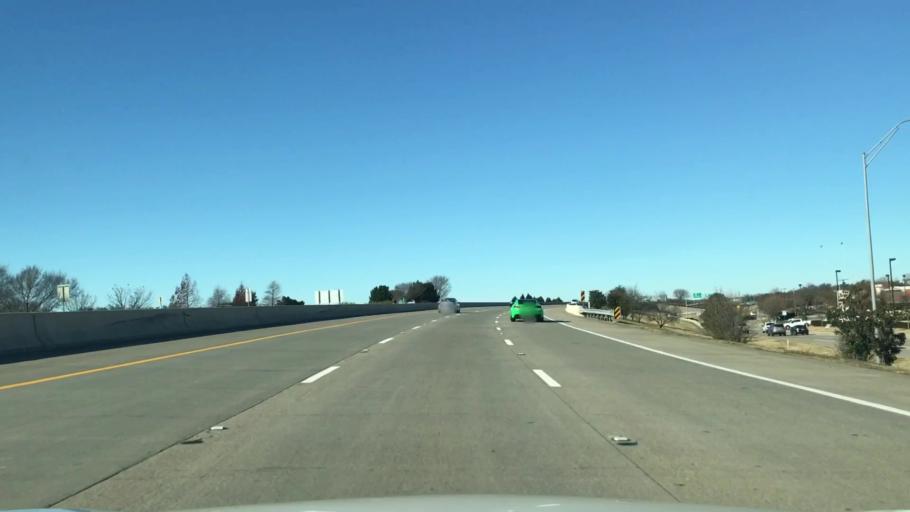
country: US
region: Texas
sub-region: Dallas County
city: Coppell
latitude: 32.9859
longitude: -96.9903
